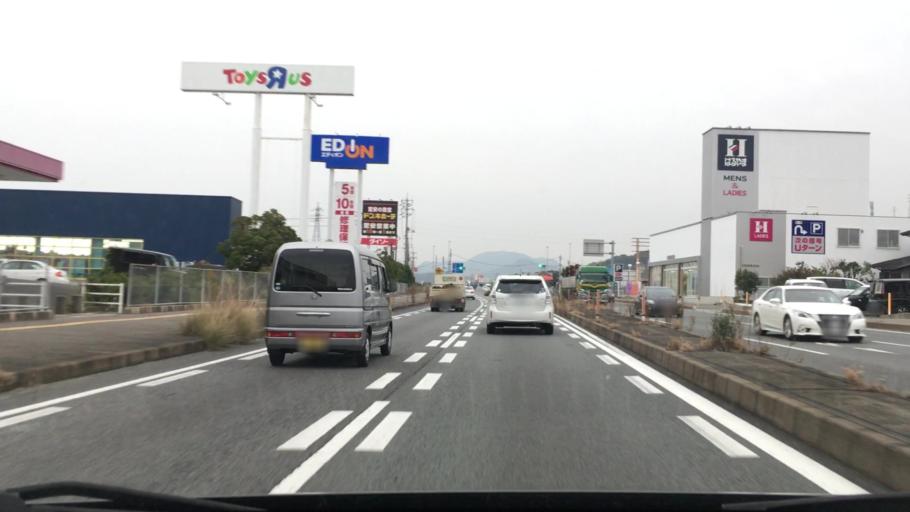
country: JP
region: Yamaguchi
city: Shimonoseki
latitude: 34.0306
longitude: 131.0120
